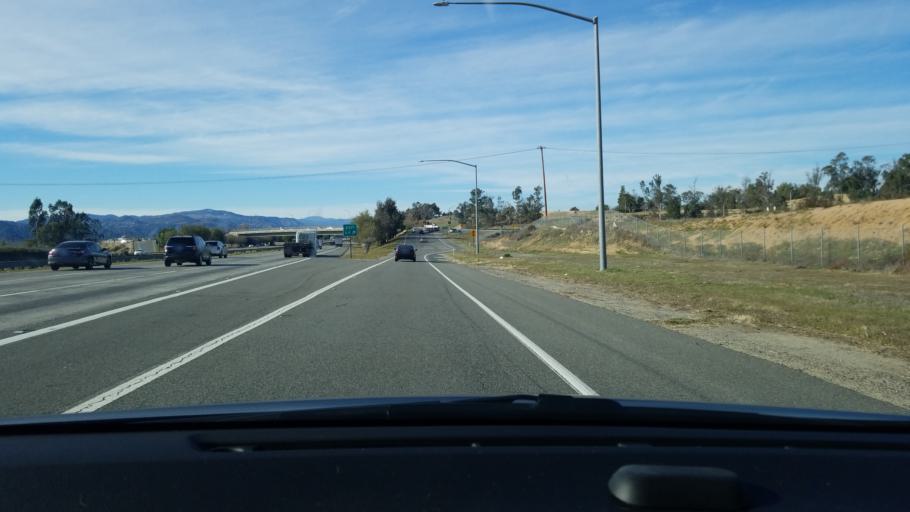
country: US
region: California
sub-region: Riverside County
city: Murrieta
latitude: 33.5529
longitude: -117.1880
